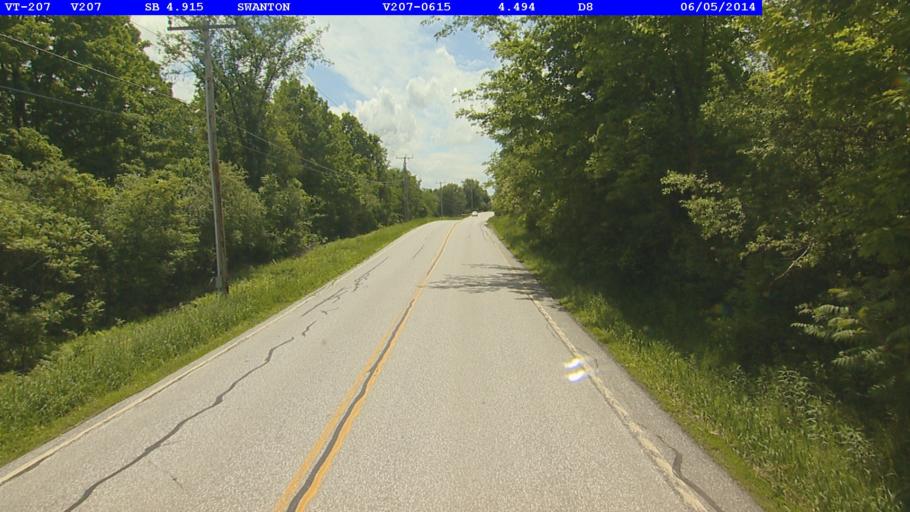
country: US
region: Vermont
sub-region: Franklin County
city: Swanton
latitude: 44.9082
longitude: -73.0619
